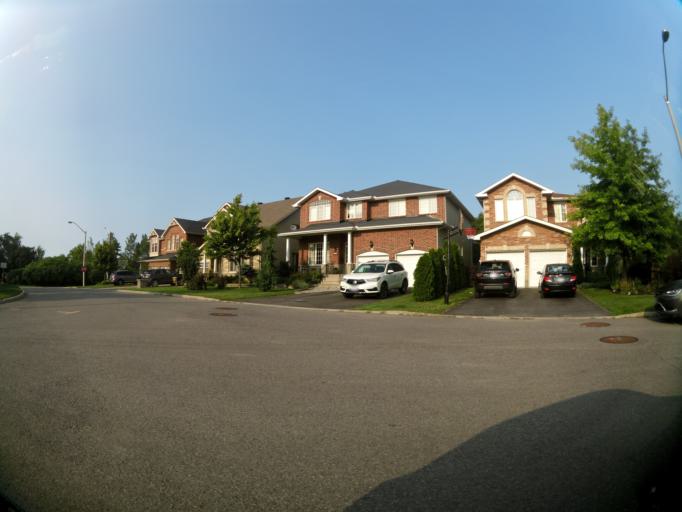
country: CA
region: Ontario
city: Clarence-Rockland
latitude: 45.4843
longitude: -75.4698
